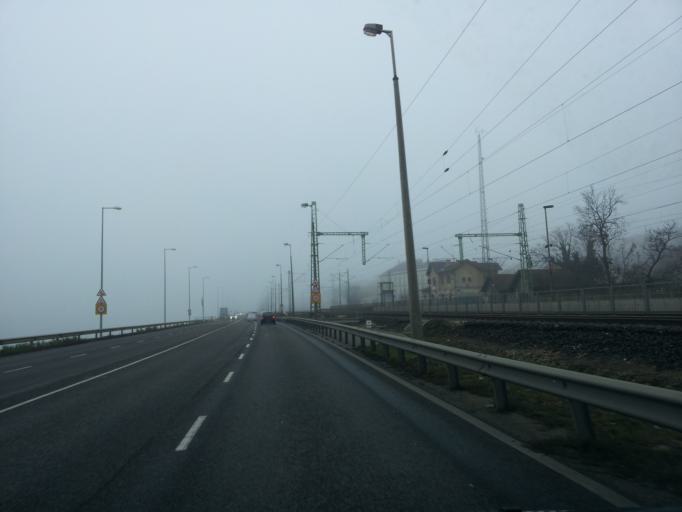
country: HU
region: Budapest
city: Budapest XXII. keruelet
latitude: 47.4249
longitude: 19.0418
